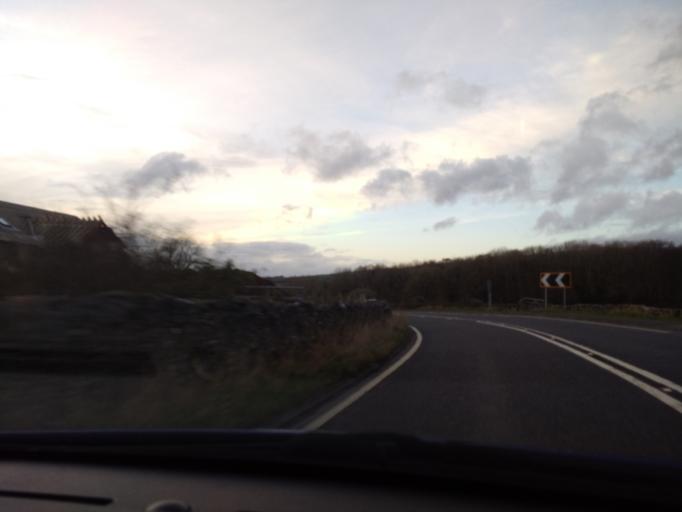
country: GB
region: England
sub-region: North Yorkshire
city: Ingleton
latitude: 54.1443
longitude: -2.4642
